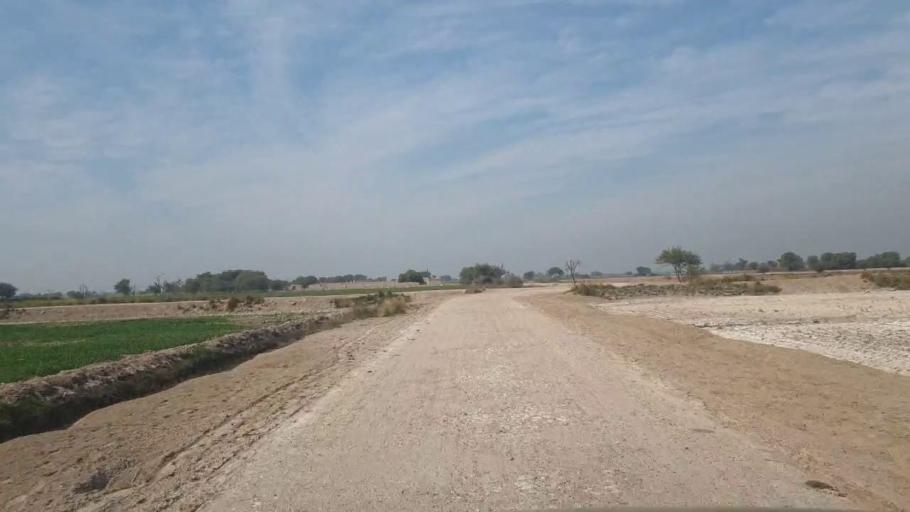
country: PK
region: Sindh
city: Nawabshah
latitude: 26.1649
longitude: 68.4997
